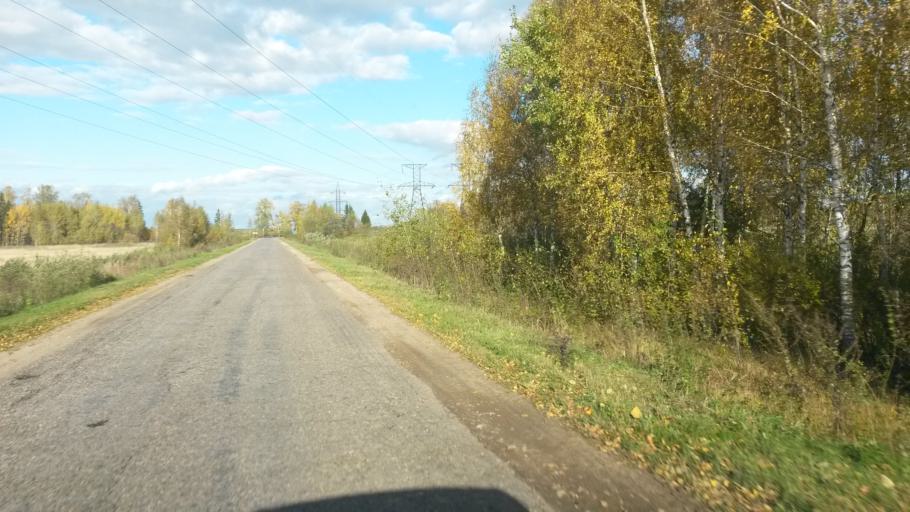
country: RU
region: Jaroslavl
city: Tunoshna
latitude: 57.5338
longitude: 40.0173
